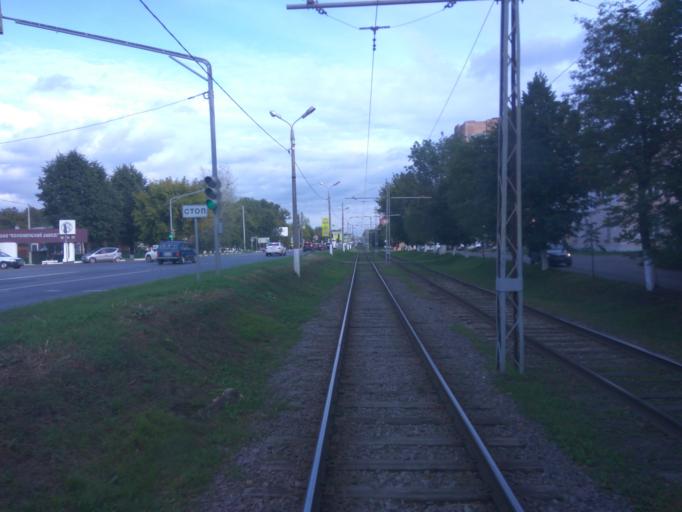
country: RU
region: Moskovskaya
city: Kolomna
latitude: 55.0881
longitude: 38.7887
